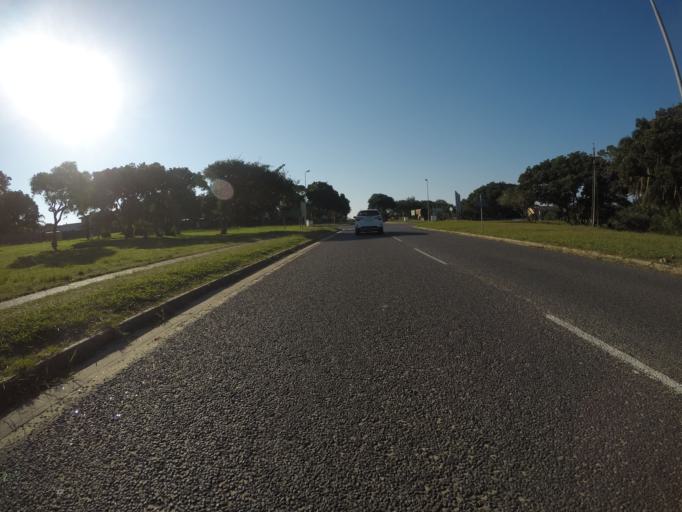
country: ZA
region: KwaZulu-Natal
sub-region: uThungulu District Municipality
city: Richards Bay
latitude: -28.7907
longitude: 32.0983
